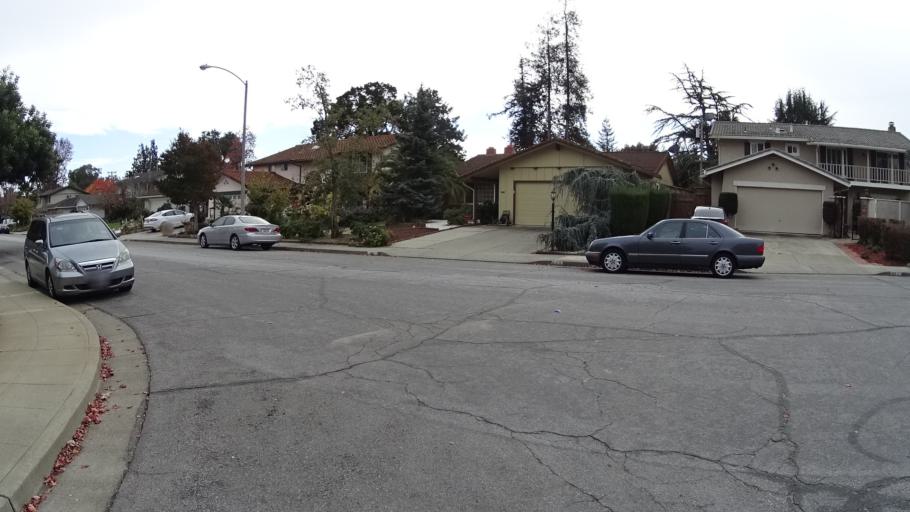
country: US
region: California
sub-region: Santa Clara County
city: Sunnyvale
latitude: 37.3598
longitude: -122.0164
